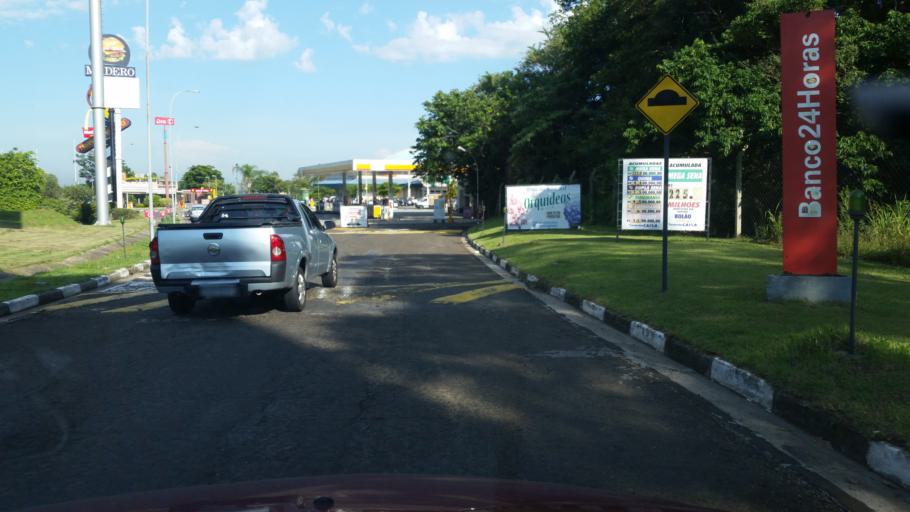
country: BR
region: Sao Paulo
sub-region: Itu
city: Itu
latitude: -23.4098
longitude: -47.2770
